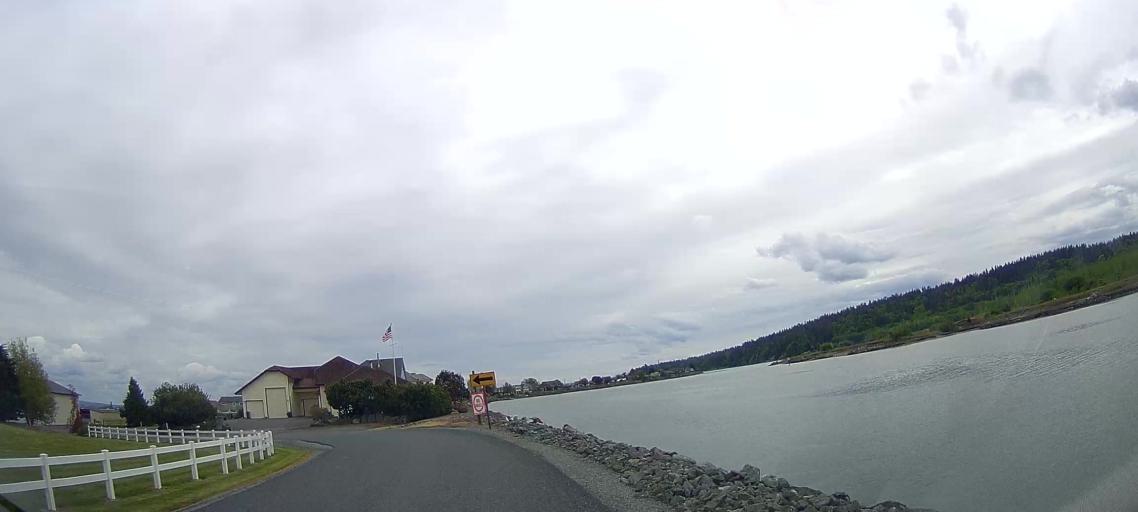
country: US
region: Washington
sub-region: Skagit County
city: Anacortes
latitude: 48.4344
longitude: -122.4984
